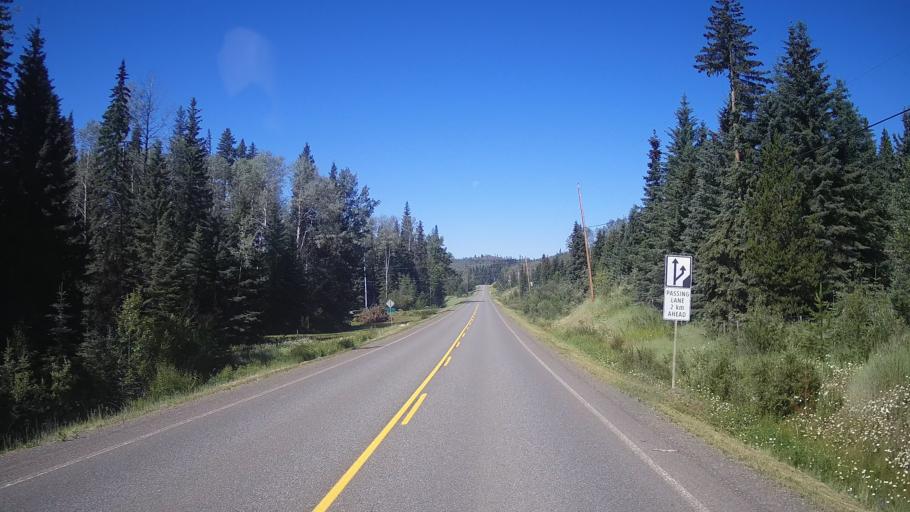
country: CA
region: British Columbia
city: Kamloops
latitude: 51.5054
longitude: -120.6088
